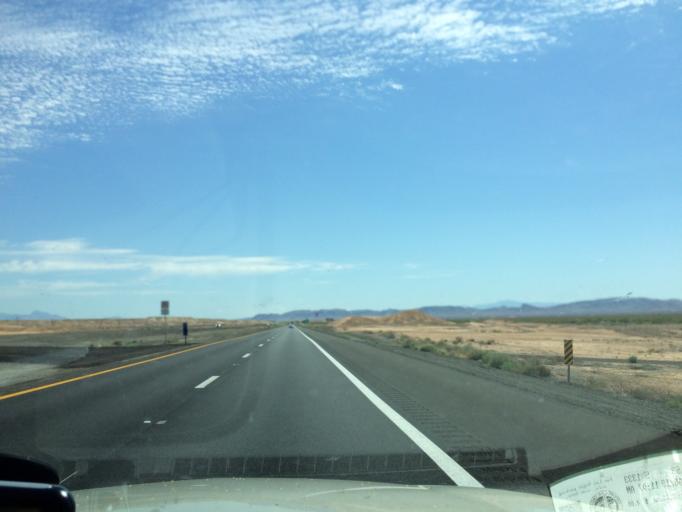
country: US
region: Nevada
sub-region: Clark County
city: Moapa Town
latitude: 36.4931
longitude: -114.7793
